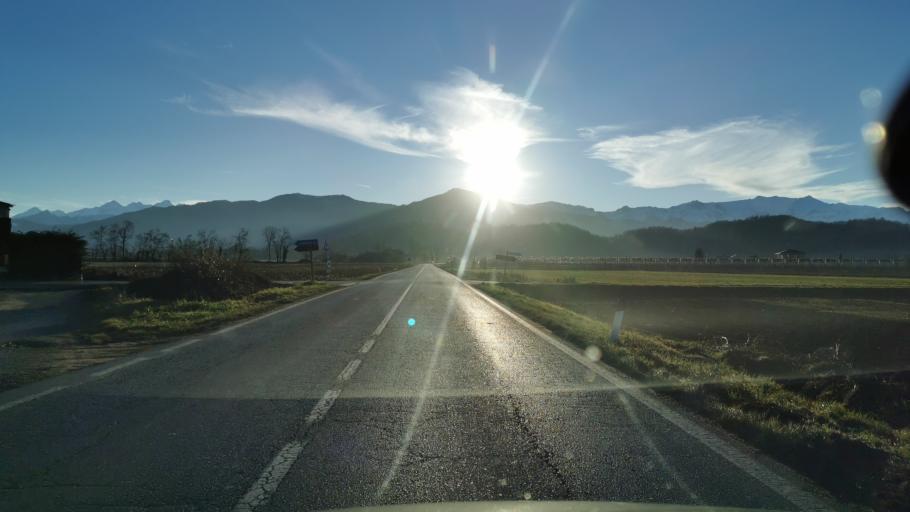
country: IT
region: Piedmont
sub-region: Provincia di Cuneo
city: Caraglio
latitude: 44.4329
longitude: 7.4422
